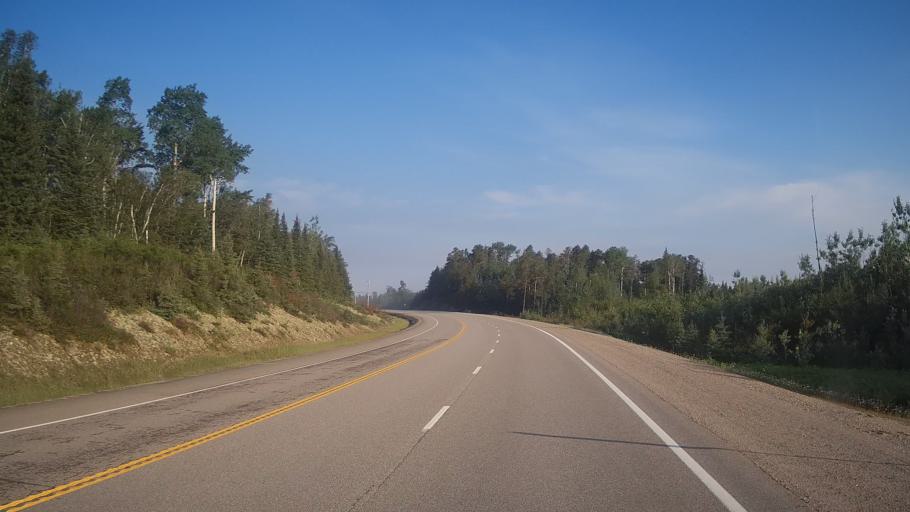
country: CA
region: Ontario
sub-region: Rainy River District
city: Atikokan
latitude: 49.3695
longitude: -91.5603
